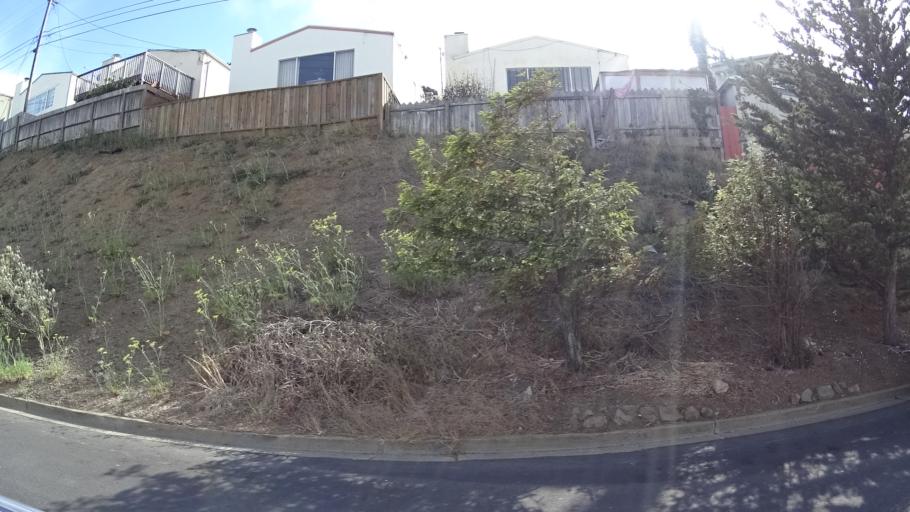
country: US
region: California
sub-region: San Mateo County
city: Daly City
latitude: 37.7072
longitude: -122.4289
